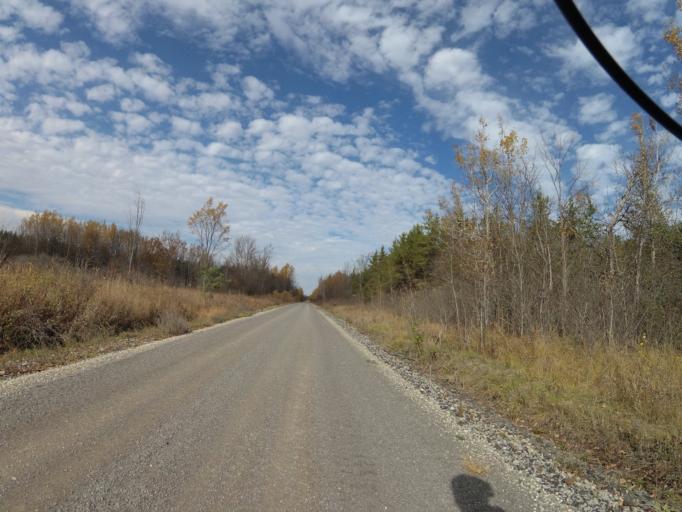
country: CA
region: Ontario
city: Carleton Place
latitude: 45.0750
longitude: -76.1014
